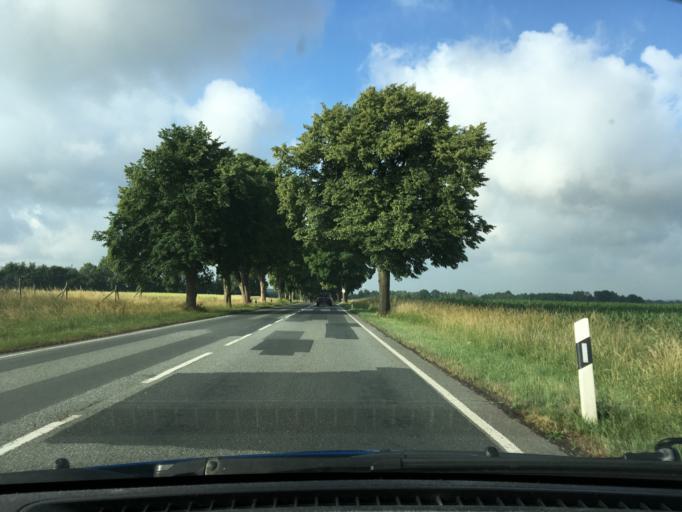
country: DE
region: Lower Saxony
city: Kakenstorf
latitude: 53.3207
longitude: 9.8089
